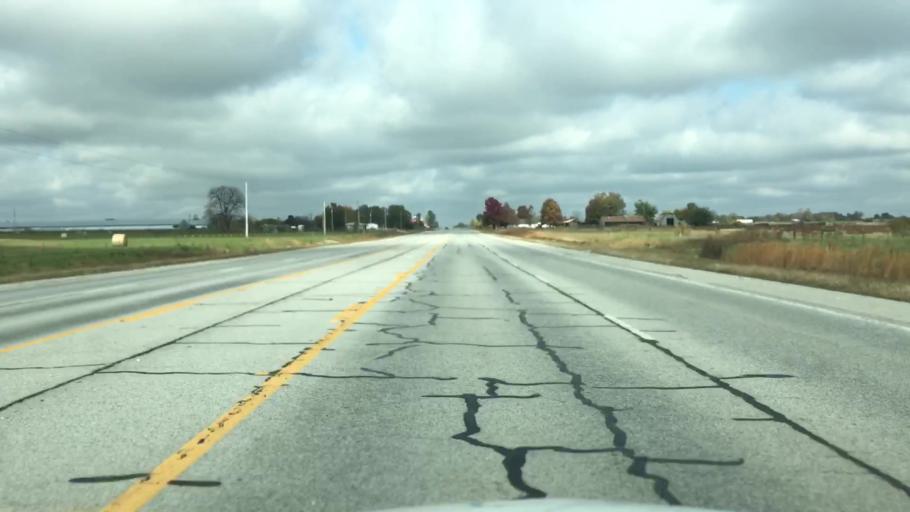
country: US
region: Arkansas
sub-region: Benton County
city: Siloam Springs
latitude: 36.2143
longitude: -94.4955
